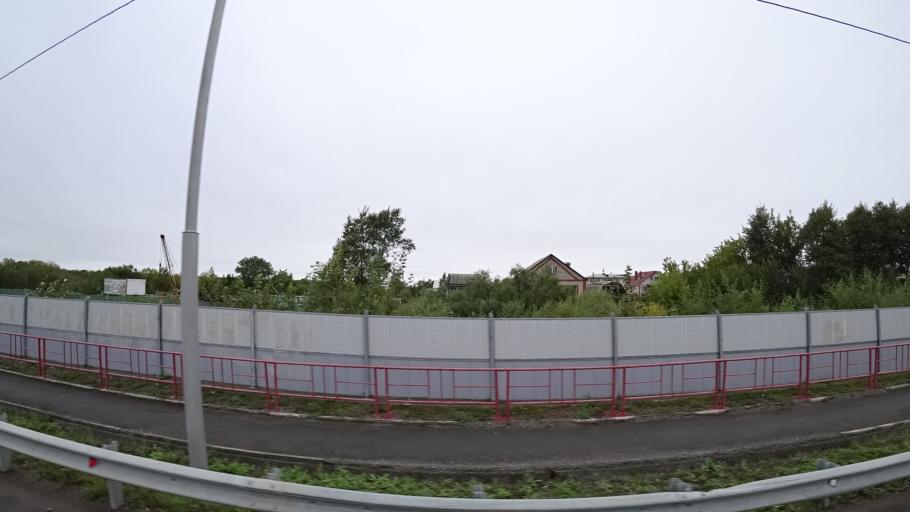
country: RU
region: Primorskiy
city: Monastyrishche
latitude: 44.1998
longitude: 132.4483
